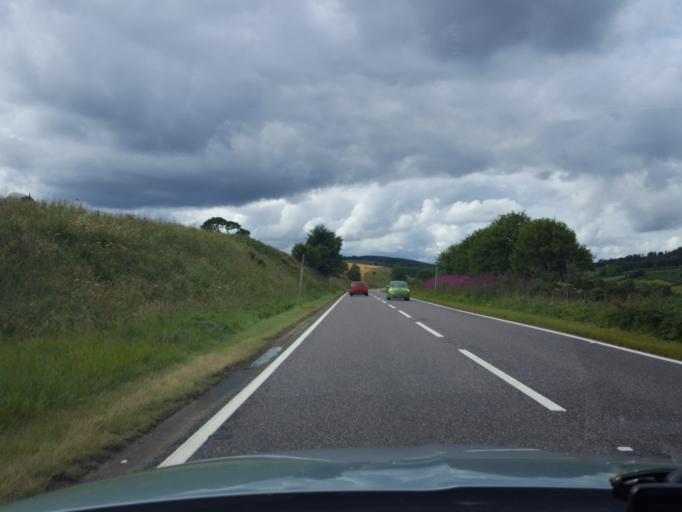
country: GB
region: Scotland
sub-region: Moray
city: Rothes
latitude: 57.4423
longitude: -3.2848
